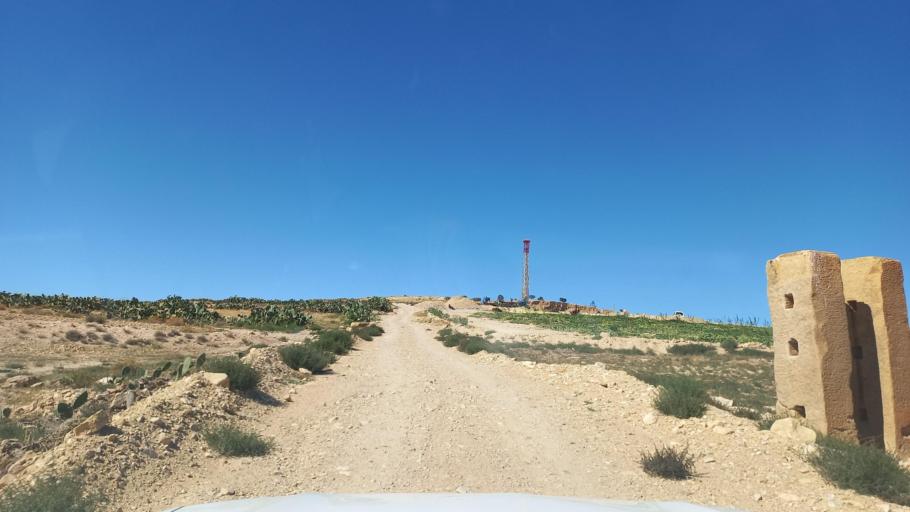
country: TN
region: Al Qasrayn
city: Sbiba
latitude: 35.3747
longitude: 9.0807
